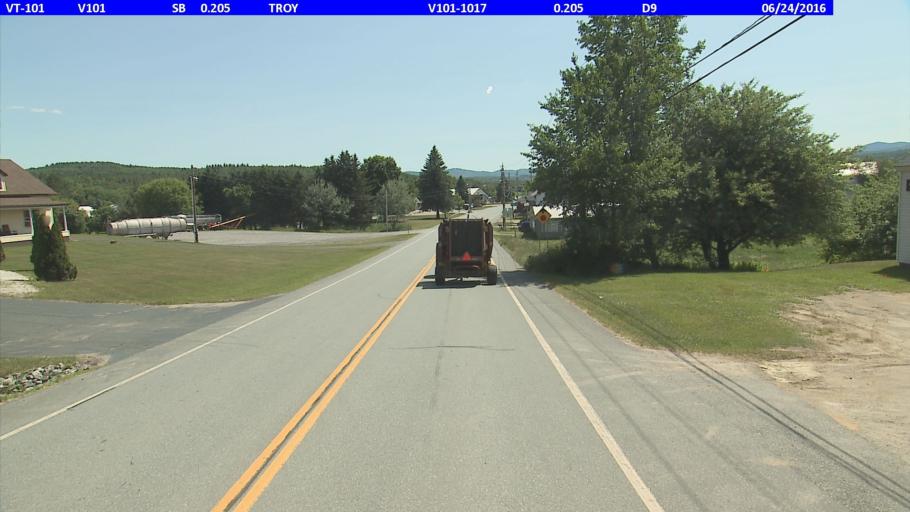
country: US
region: Vermont
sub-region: Orleans County
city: Newport
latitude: 44.9064
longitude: -72.4052
